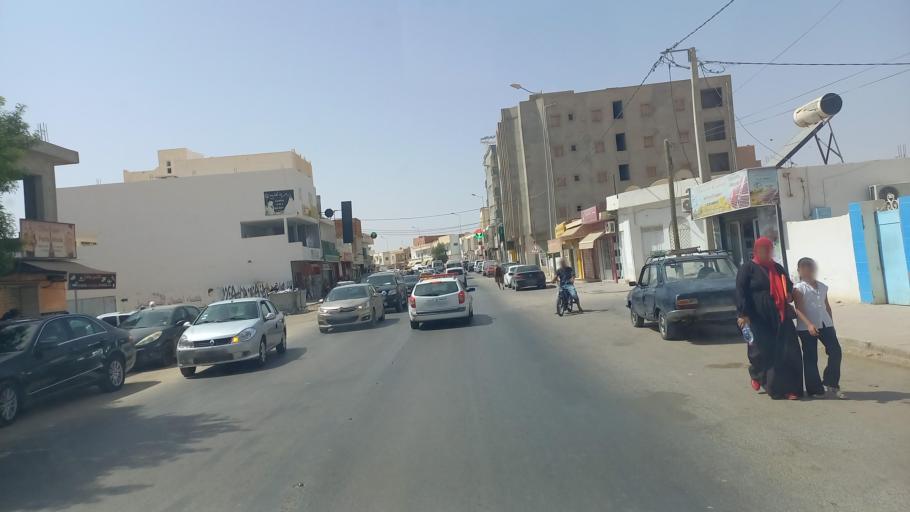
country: TN
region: Madanin
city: Medenine
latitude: 33.3378
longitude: 10.4863
